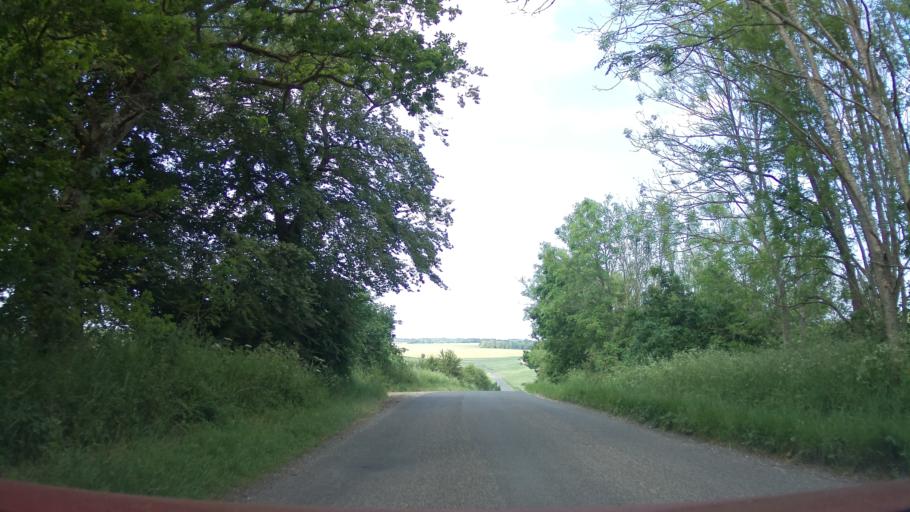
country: GB
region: England
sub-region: Wiltshire
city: Milston
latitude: 51.2594
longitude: -1.7297
